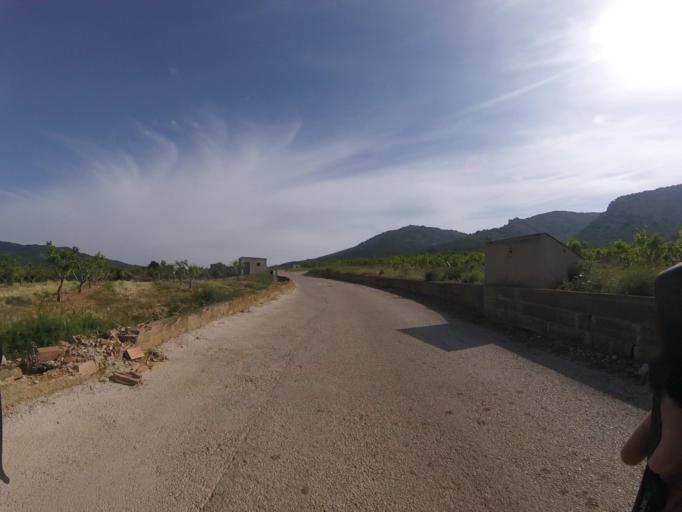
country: ES
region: Valencia
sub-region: Provincia de Castello
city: Alcala de Xivert
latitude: 40.2862
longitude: 0.2667
